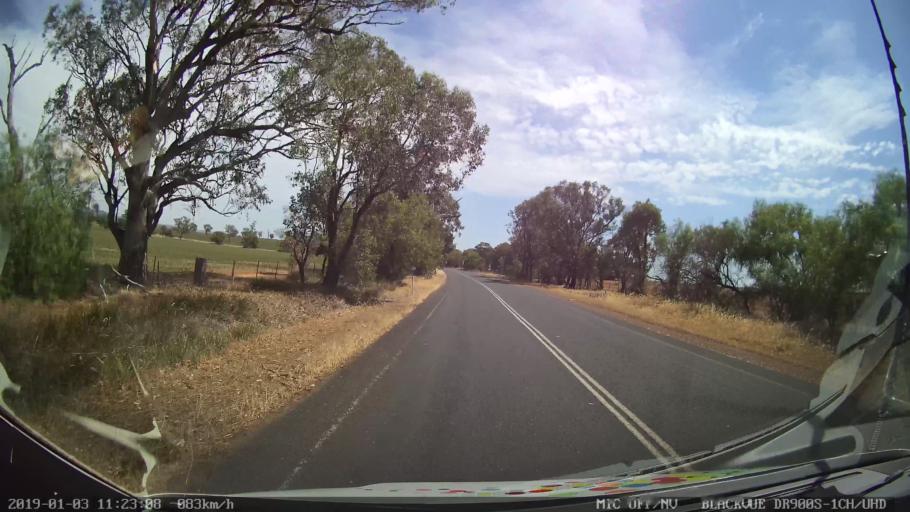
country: AU
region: New South Wales
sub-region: Weddin
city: Grenfell
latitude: -34.0669
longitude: 148.2441
